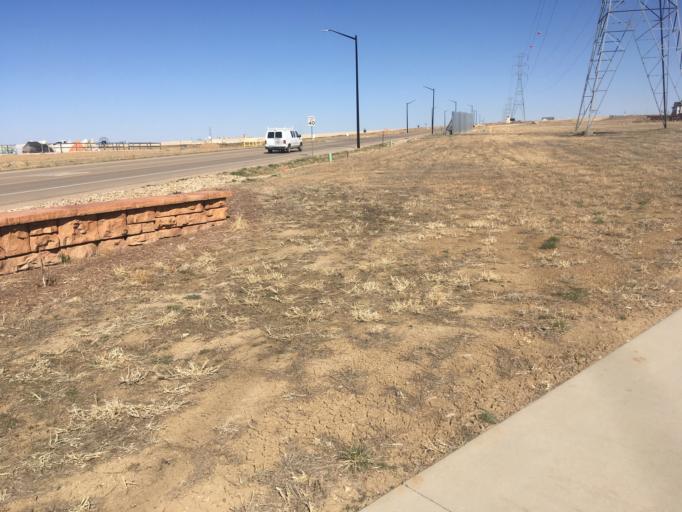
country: US
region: Colorado
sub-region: Boulder County
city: Erie
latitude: 40.0581
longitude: -105.0291
